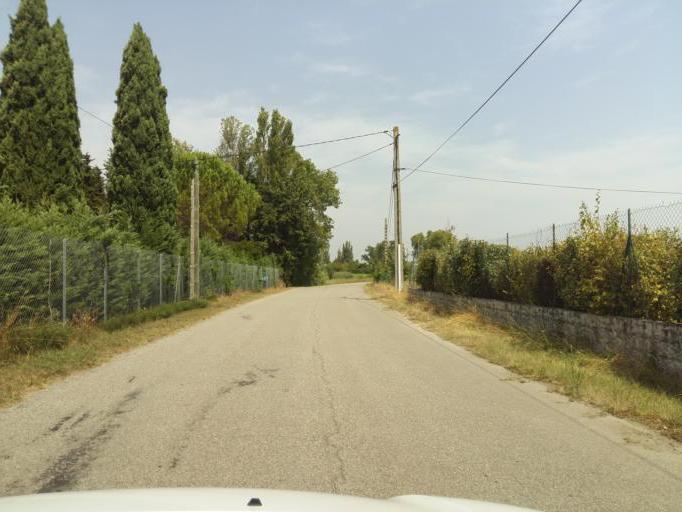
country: FR
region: Provence-Alpes-Cote d'Azur
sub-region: Departement du Vaucluse
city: Lapalud
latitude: 44.3042
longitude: 4.6820
